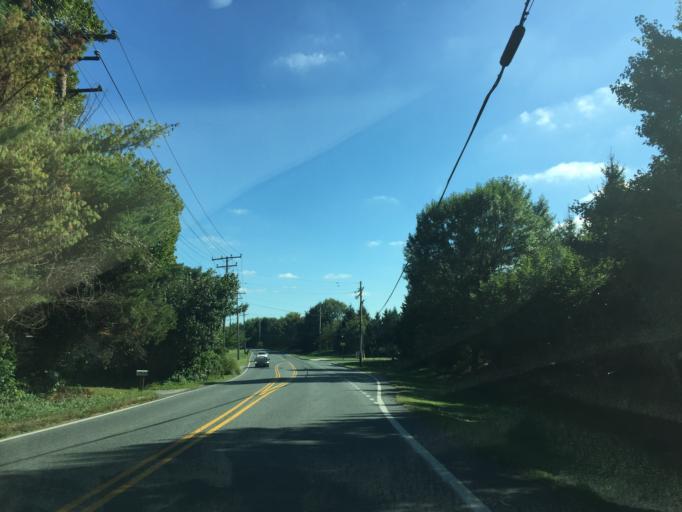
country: US
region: Maryland
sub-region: Harford County
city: Bel Air North
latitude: 39.5784
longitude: -76.3645
